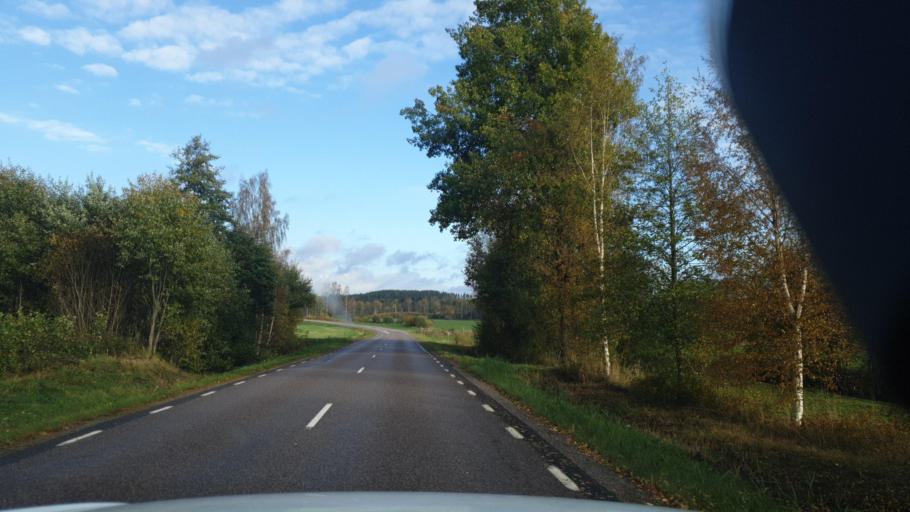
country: SE
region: Vaermland
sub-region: Arvika Kommun
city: Arvika
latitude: 59.4947
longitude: 12.6848
